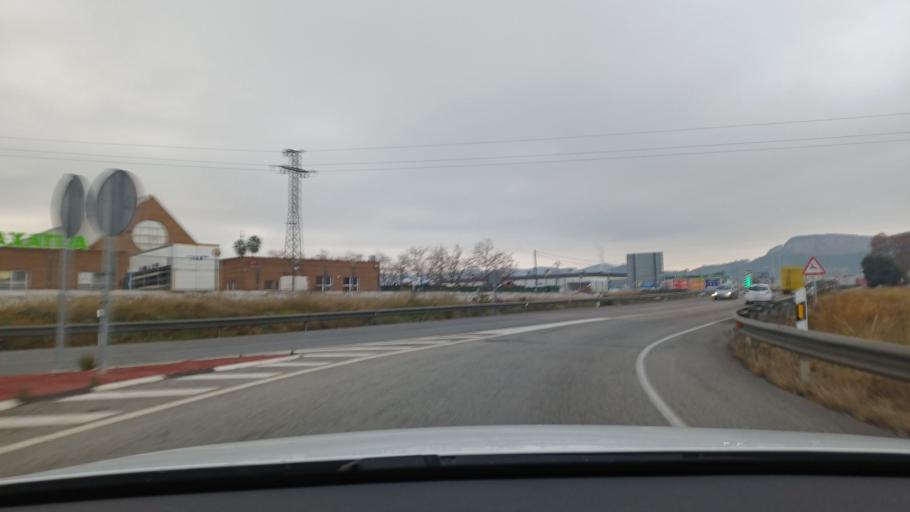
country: ES
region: Valencia
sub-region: Provincia de Valencia
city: Llosa de Ranes
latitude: 39.0017
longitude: -0.5288
